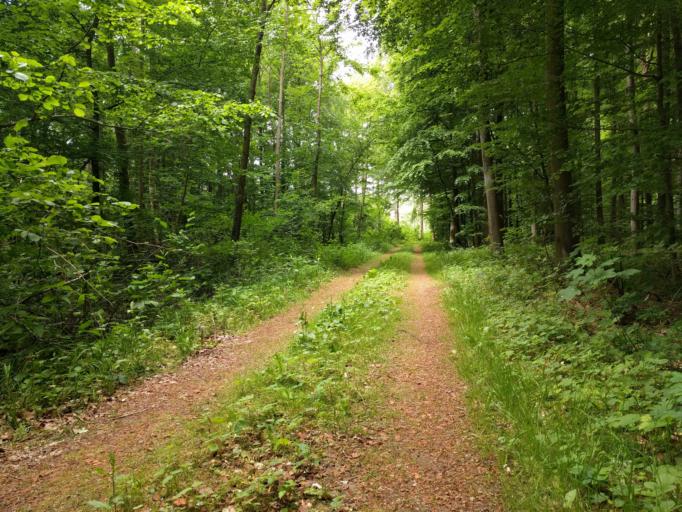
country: DK
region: South Denmark
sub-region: Kerteminde Kommune
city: Kerteminde
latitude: 55.4245
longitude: 10.6138
